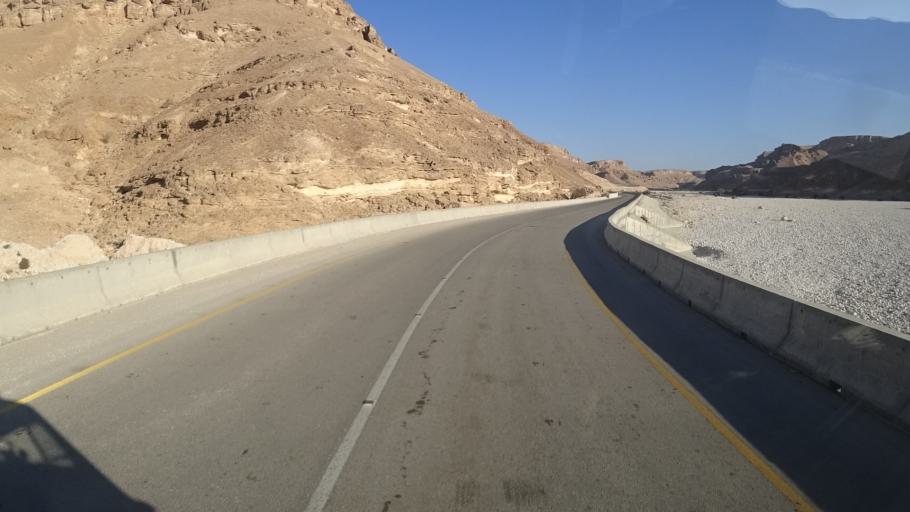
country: YE
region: Al Mahrah
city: Hawf
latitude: 17.0984
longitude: 53.0513
